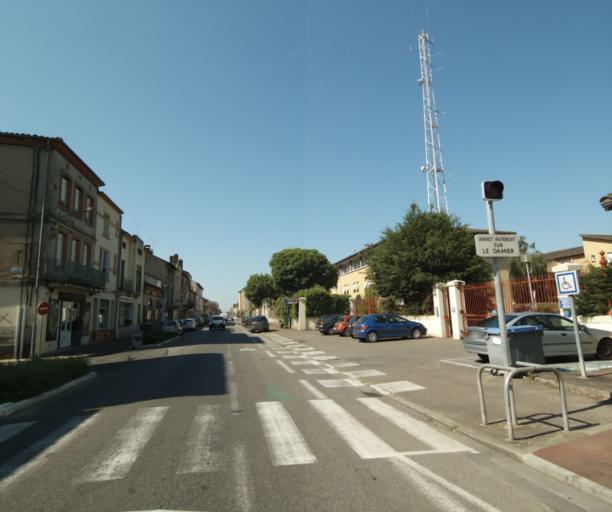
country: FR
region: Midi-Pyrenees
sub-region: Departement du Tarn-et-Garonne
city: Montauban
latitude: 44.0122
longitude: 1.3459
